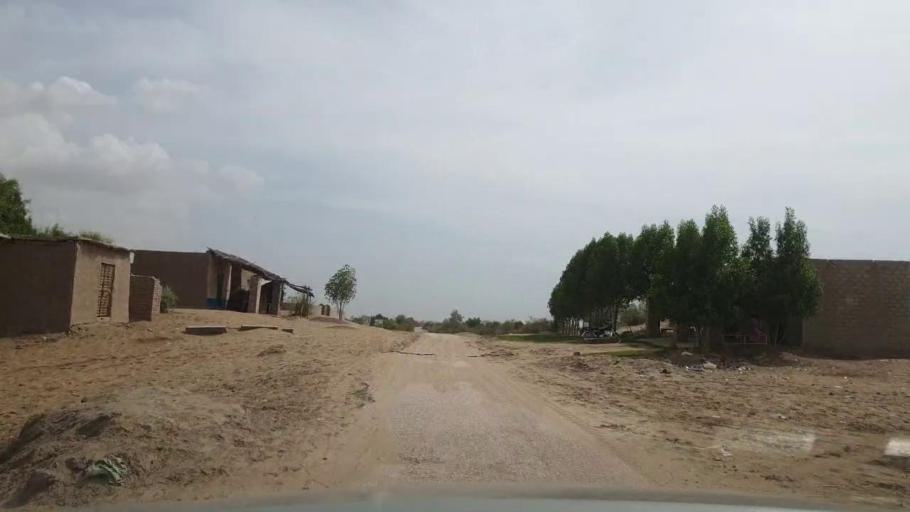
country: PK
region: Sindh
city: Bozdar
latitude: 27.1042
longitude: 69.0202
